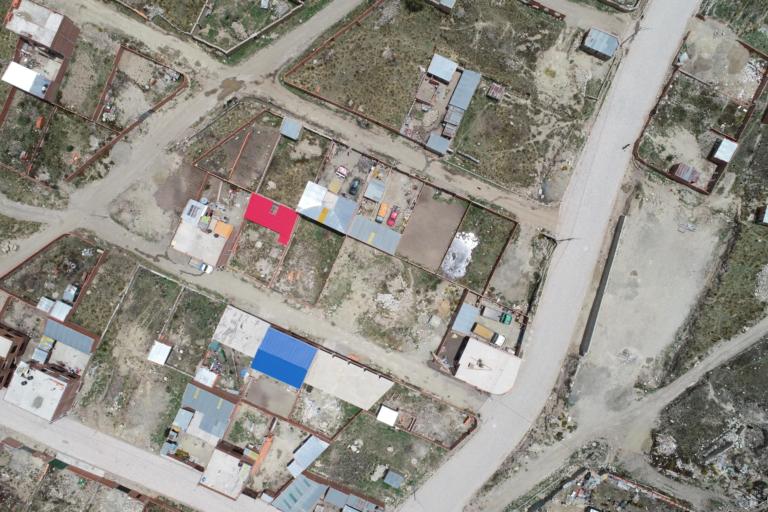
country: BO
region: La Paz
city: La Paz
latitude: -16.4389
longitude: -68.1426
